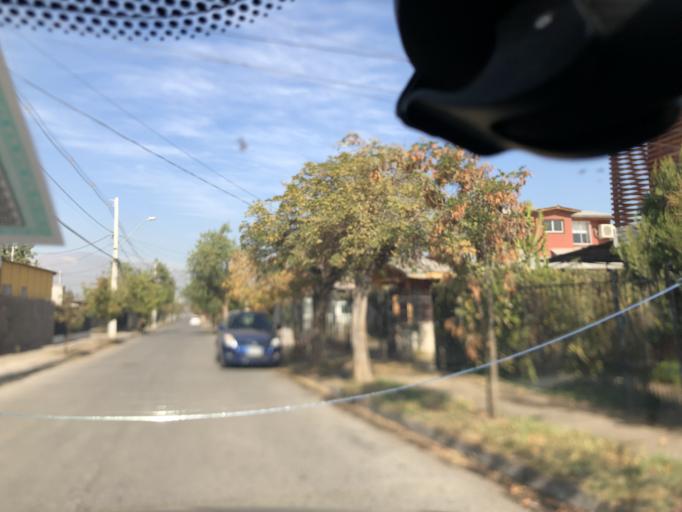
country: CL
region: Santiago Metropolitan
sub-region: Provincia de Cordillera
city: Puente Alto
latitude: -33.6139
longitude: -70.5663
